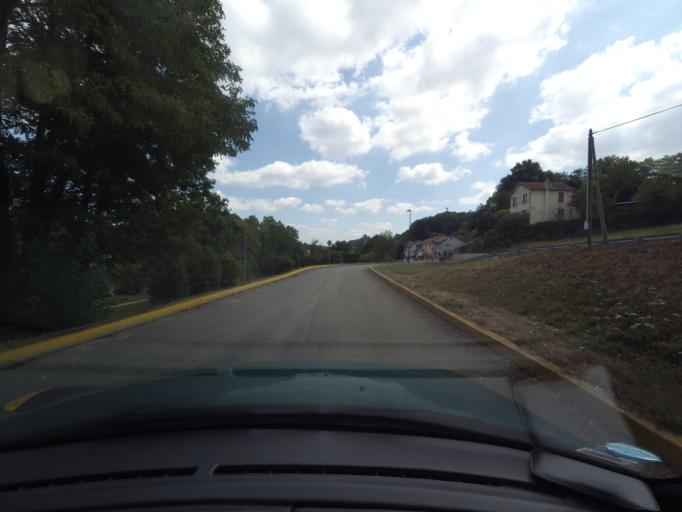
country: FR
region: Limousin
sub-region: Departement de la Haute-Vienne
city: Isle
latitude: 45.7815
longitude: 1.1897
